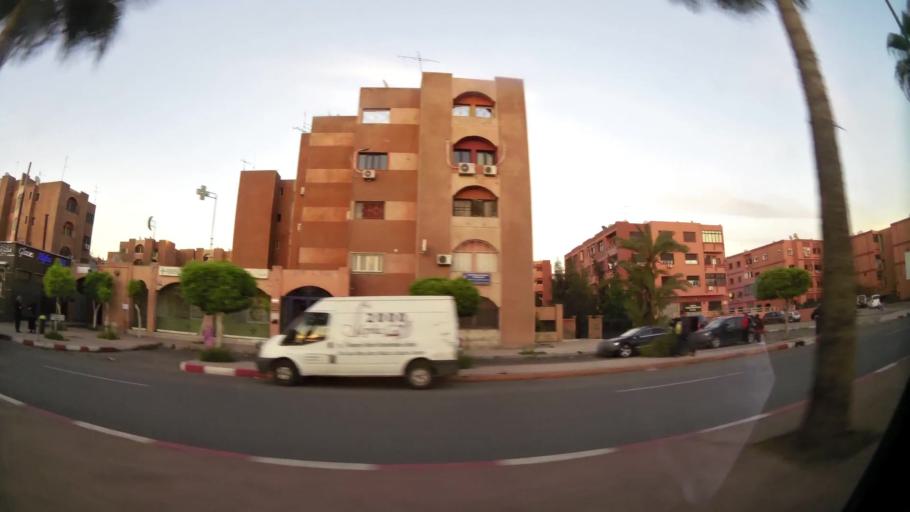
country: MA
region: Marrakech-Tensift-Al Haouz
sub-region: Marrakech
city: Marrakesh
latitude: 31.6430
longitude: -8.0003
